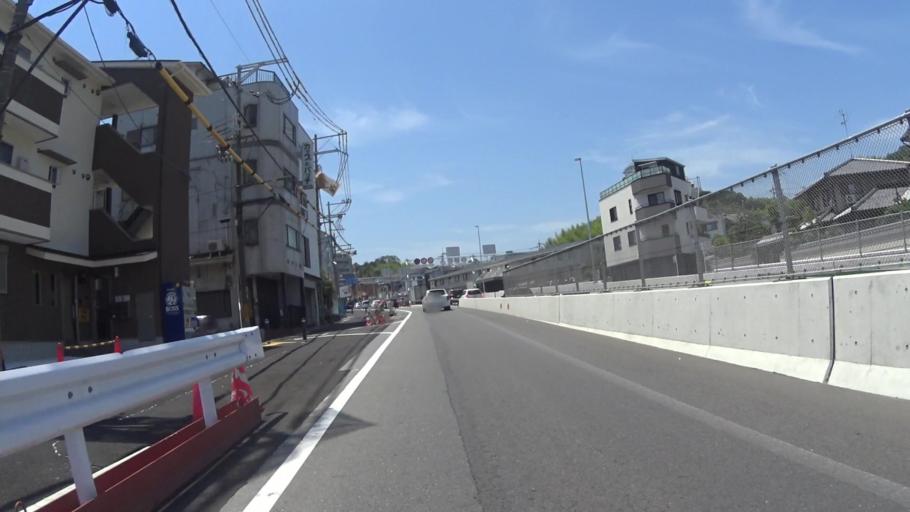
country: JP
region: Kyoto
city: Muko
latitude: 34.9805
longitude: 135.6913
